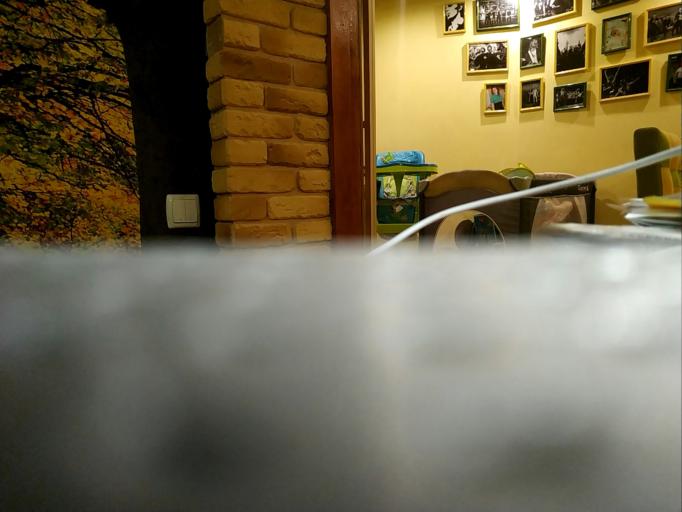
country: RU
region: Tverskaya
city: Spirovo
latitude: 57.3396
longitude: 35.0583
